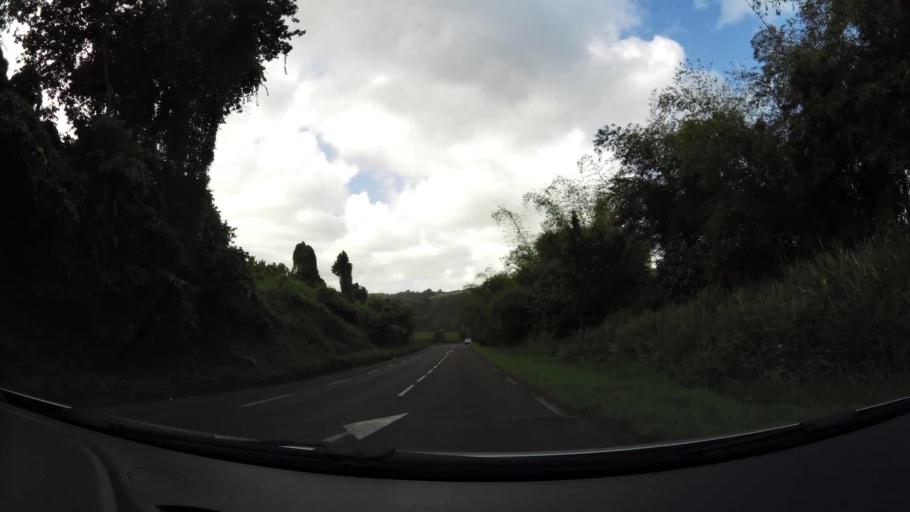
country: MQ
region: Martinique
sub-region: Martinique
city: Le Lorrain
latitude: 14.8257
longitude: -61.0396
